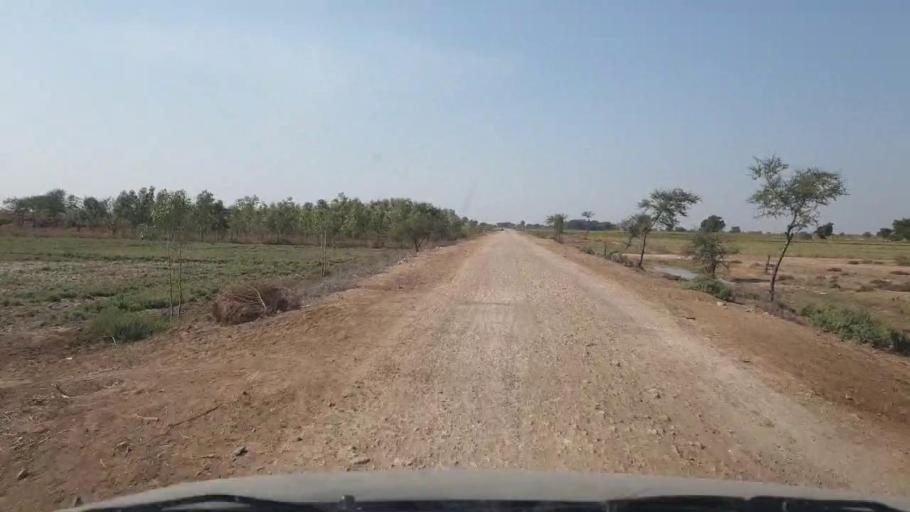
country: PK
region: Sindh
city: Samaro
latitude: 25.1929
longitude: 69.3473
